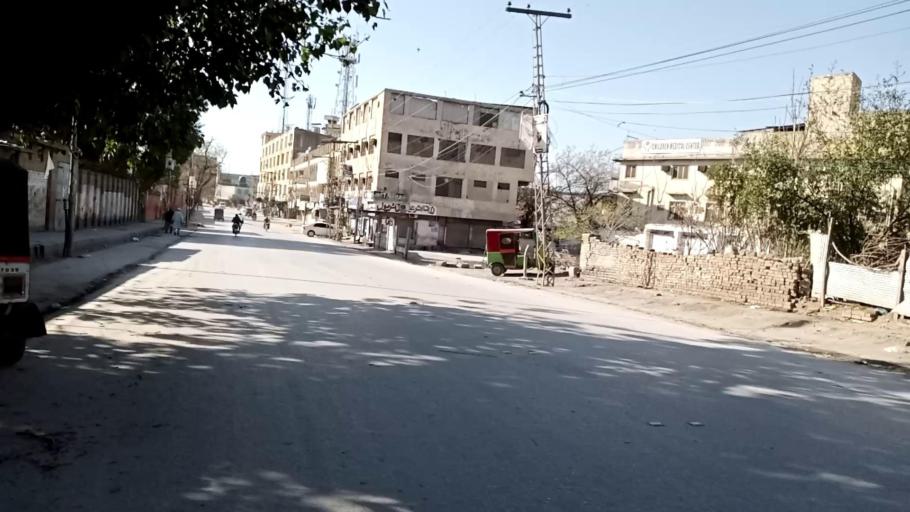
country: PK
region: Khyber Pakhtunkhwa
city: Peshawar
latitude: 34.0036
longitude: 71.5594
